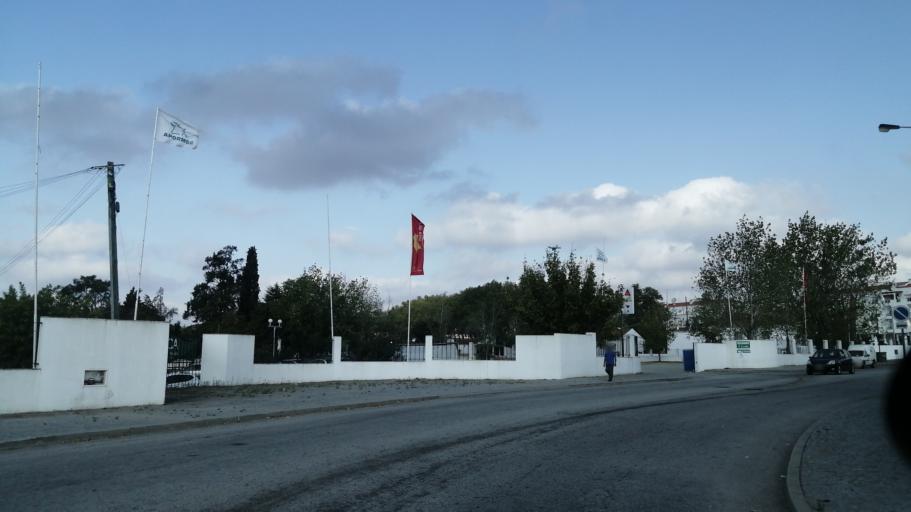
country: PT
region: Evora
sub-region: Montemor-O-Novo
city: Montemor-o-Novo
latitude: 38.6448
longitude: -8.2032
